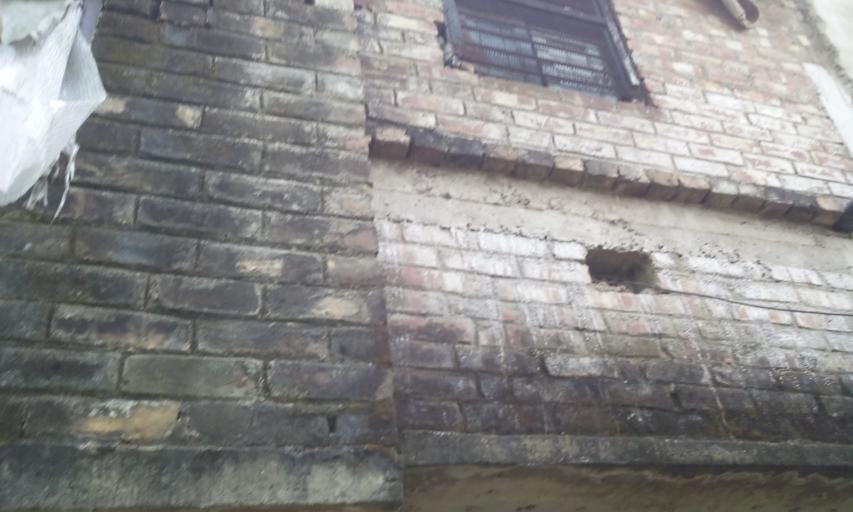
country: IN
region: West Bengal
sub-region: Haora
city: Bankra
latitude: 22.6180
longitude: 88.2705
